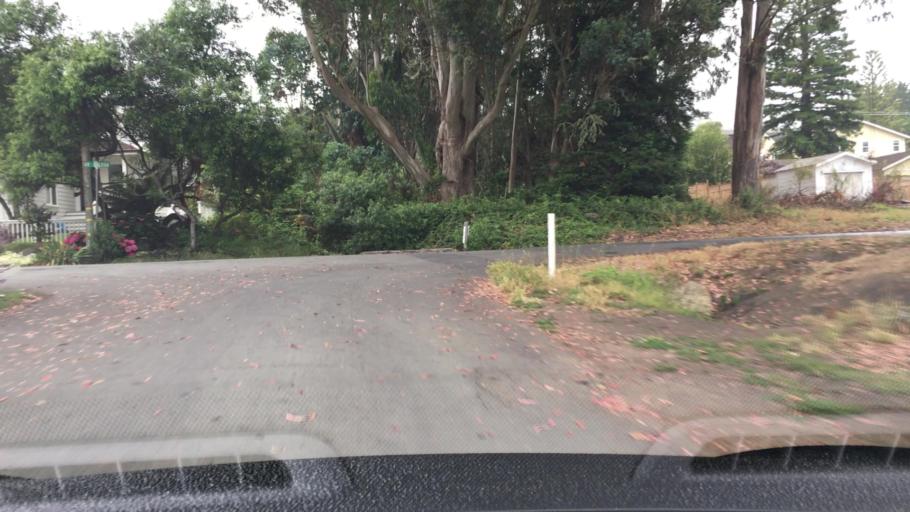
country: US
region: California
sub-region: San Mateo County
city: El Granada
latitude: 37.5074
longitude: -122.4751
